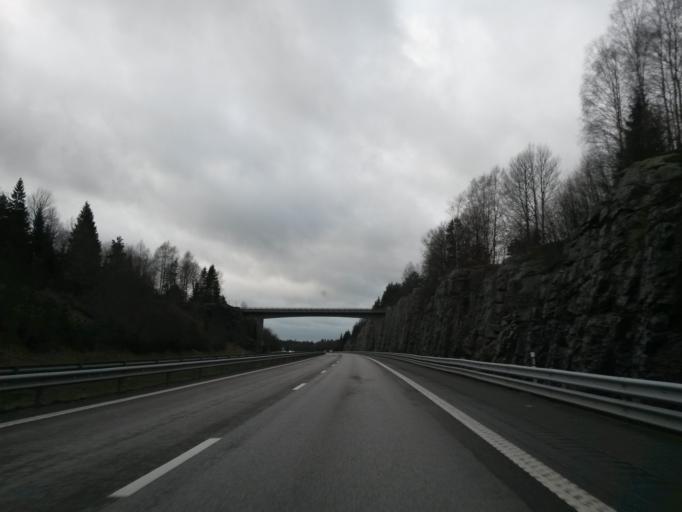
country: SE
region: Vaestra Goetaland
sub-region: Boras Kommun
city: Sandared
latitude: 57.6809
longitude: 12.7175
